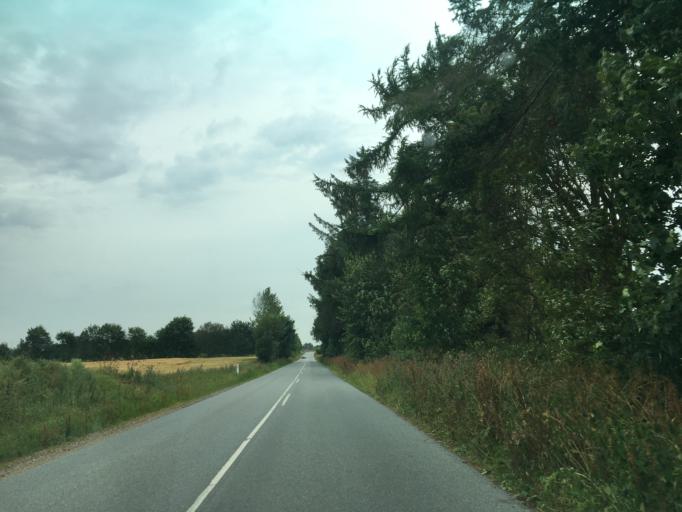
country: DK
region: North Denmark
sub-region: Thisted Kommune
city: Hurup
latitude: 56.7990
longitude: 8.4112
